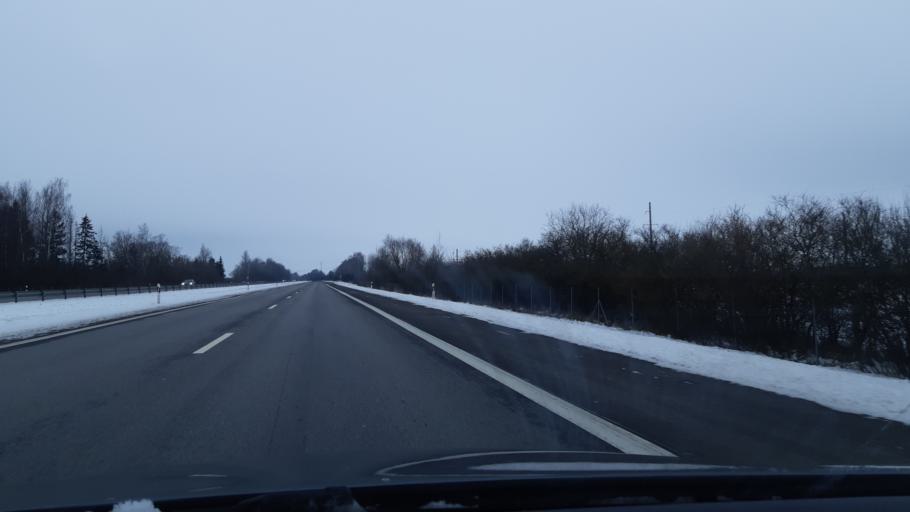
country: LT
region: Kauno apskritis
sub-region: Kaunas
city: Sargenai
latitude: 55.0774
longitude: 23.8137
